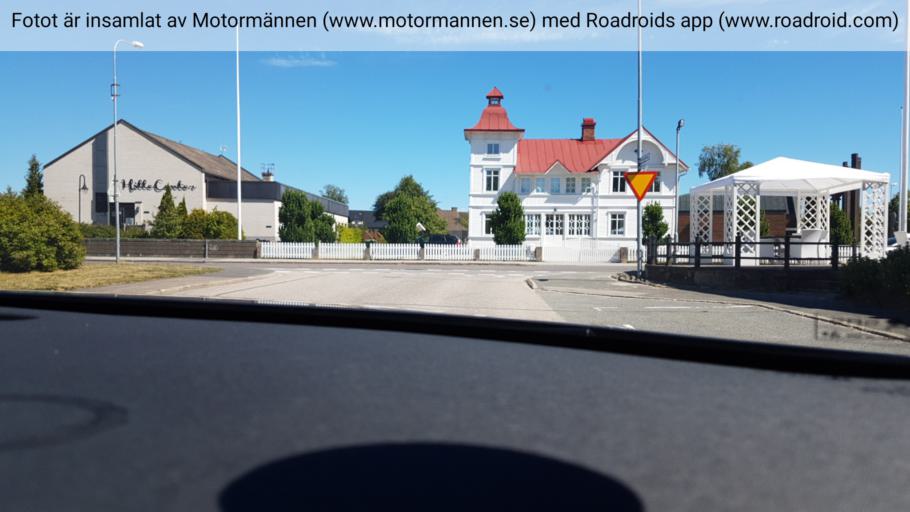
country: SE
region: Joenkoeping
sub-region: Gnosjo Kommun
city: Hillerstorp
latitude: 57.3154
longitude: 13.8802
